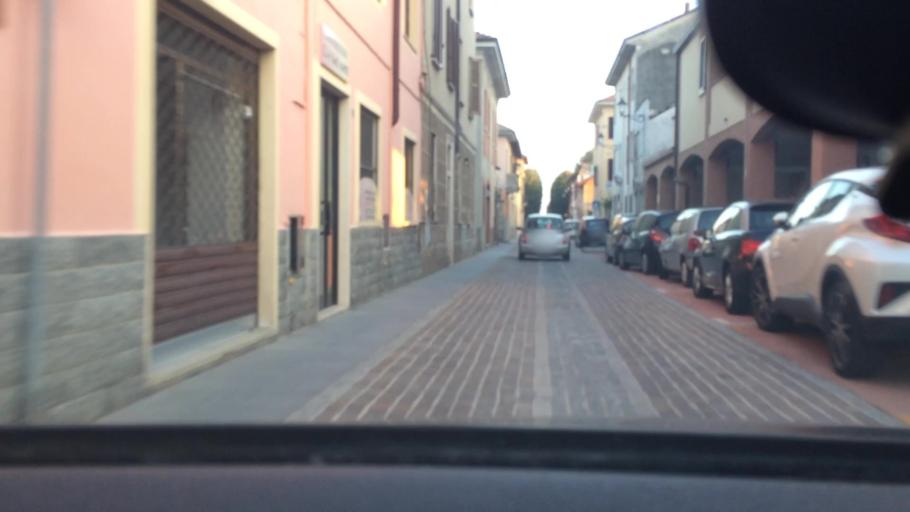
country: IT
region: Lombardy
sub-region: Provincia di Monza e Brianza
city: Ceriano Laghetto
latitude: 45.6276
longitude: 9.0801
